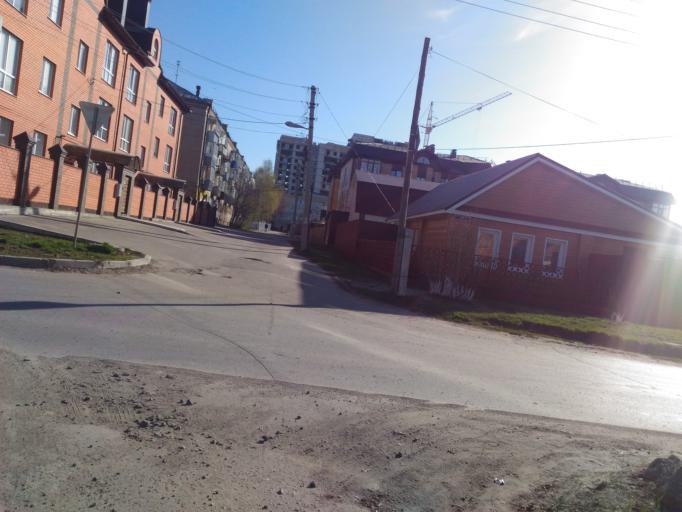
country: RU
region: Ulyanovsk
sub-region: Ulyanovskiy Rayon
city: Ulyanovsk
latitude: 54.3455
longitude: 48.3818
